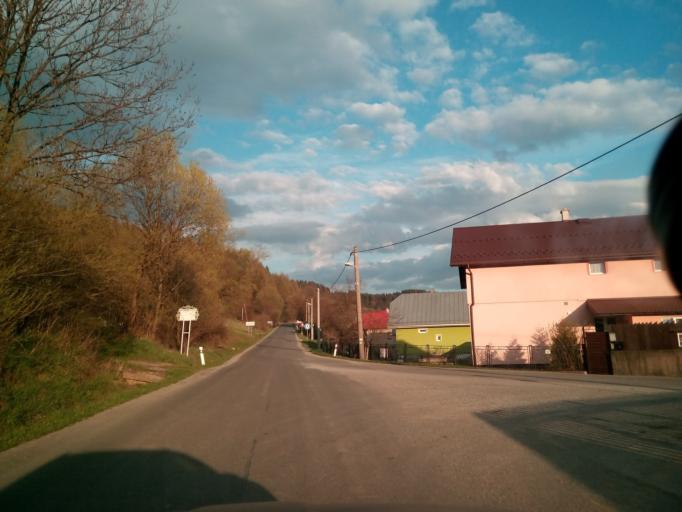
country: PL
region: Lesser Poland Voivodeship
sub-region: Powiat nowotarski
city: Niedzica
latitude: 49.3388
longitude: 20.2929
